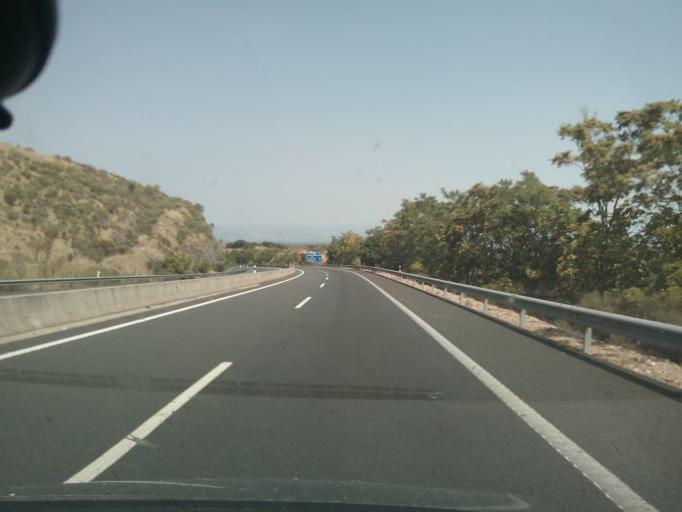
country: ES
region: Extremadura
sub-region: Provincia de Caceres
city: Romangordo
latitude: 39.7492
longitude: -5.7266
